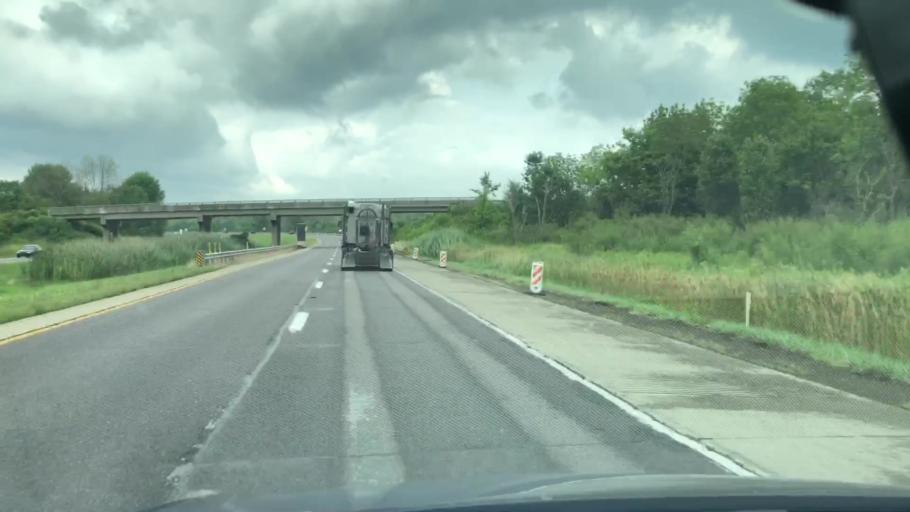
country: US
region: Pennsylvania
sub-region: Erie County
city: Erie
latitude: 42.0203
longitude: -80.1314
